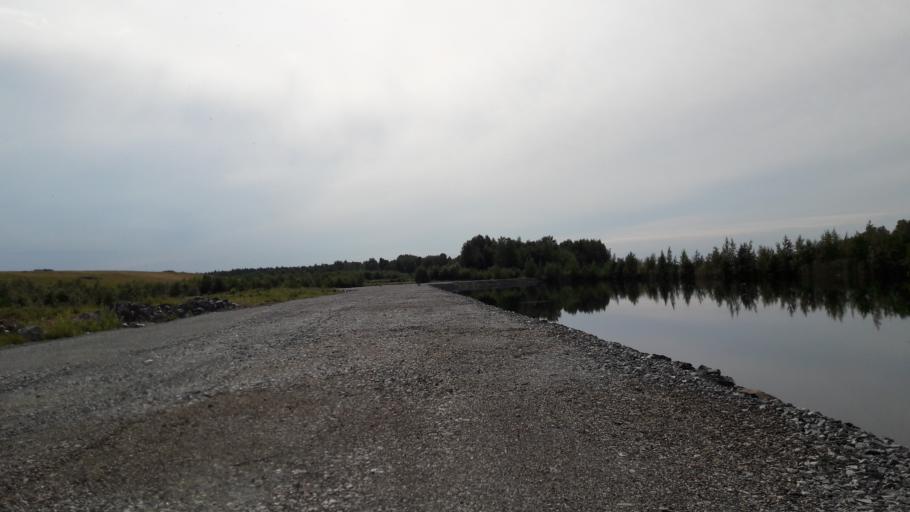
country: FI
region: North Karelia
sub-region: Joensuu
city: Joensuu
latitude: 62.5914
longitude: 29.7540
